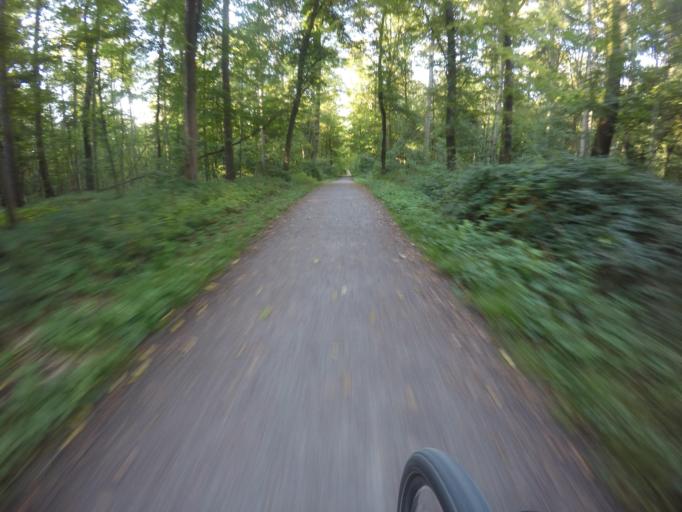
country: DE
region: Baden-Wuerttemberg
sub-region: Regierungsbezirk Stuttgart
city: Stuttgart Feuerbach
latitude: 48.8195
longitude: 9.1509
